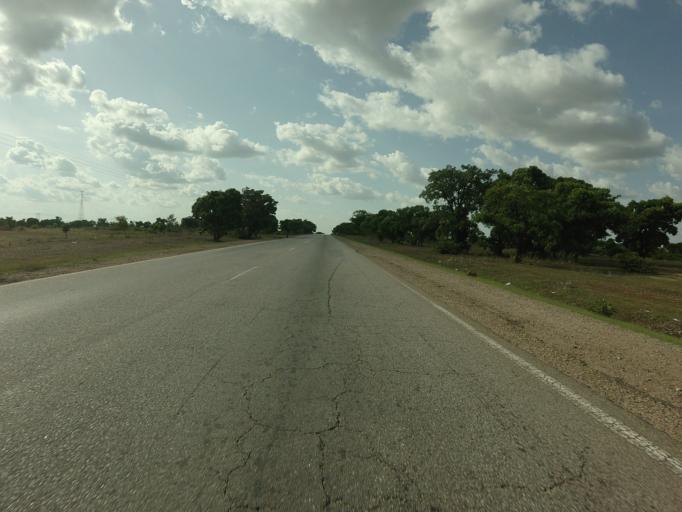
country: GH
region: Upper East
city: Bolgatanga
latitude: 10.6617
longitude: -0.8594
